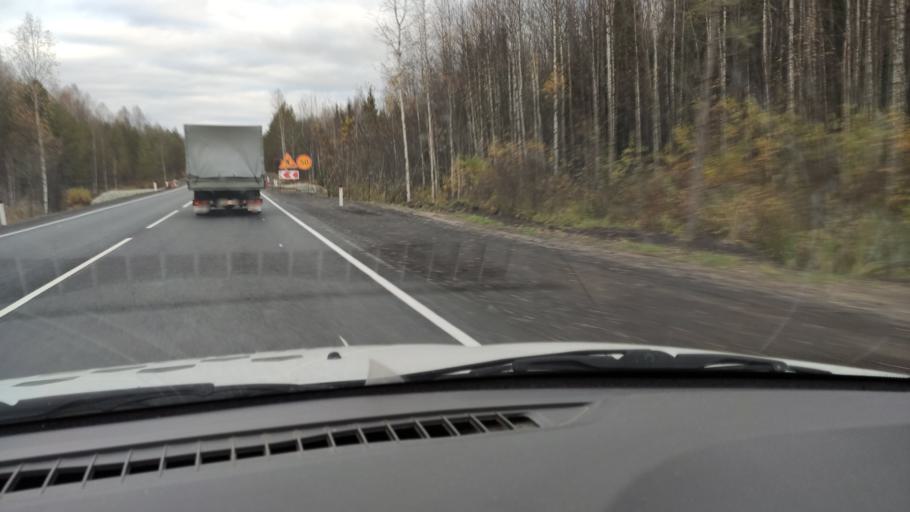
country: RU
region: Kirov
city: Chernaya Kholunitsa
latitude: 58.8746
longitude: 51.4937
